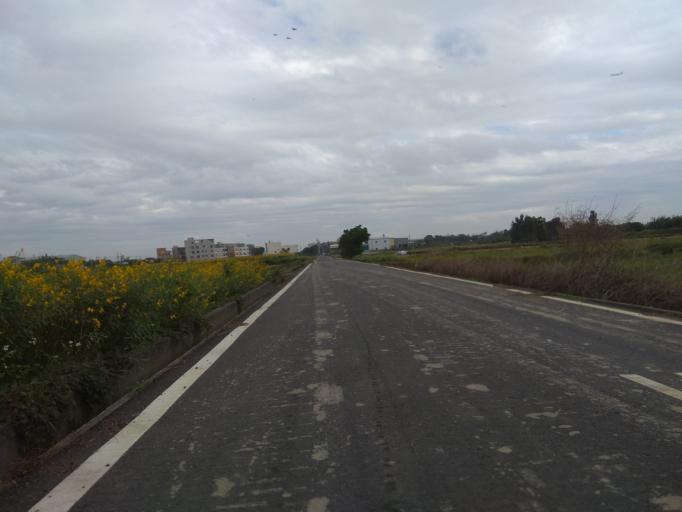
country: TW
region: Taiwan
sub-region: Hsinchu
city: Zhubei
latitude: 24.9845
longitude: 121.0485
